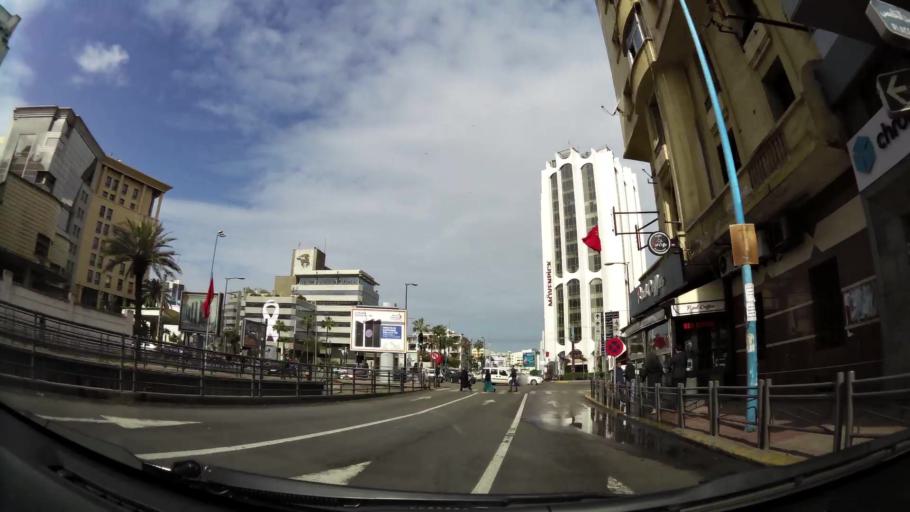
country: MA
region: Grand Casablanca
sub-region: Casablanca
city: Casablanca
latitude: 33.5834
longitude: -7.6226
